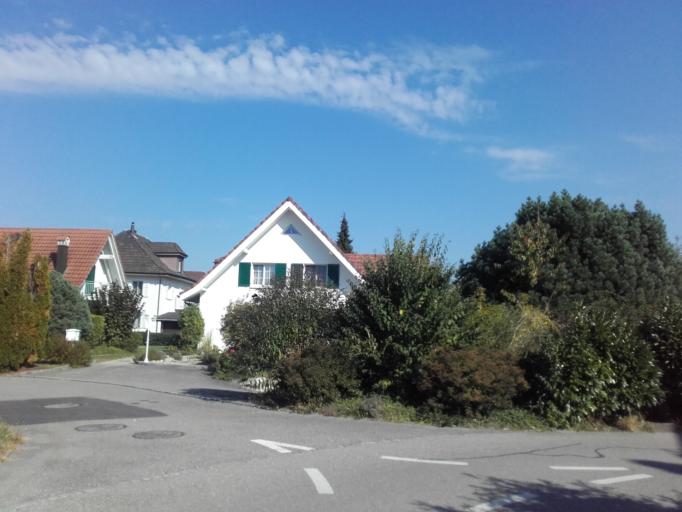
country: CH
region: Solothurn
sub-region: Bezirk Wasseramt
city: Luterbach
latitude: 47.2155
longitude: 7.5821
